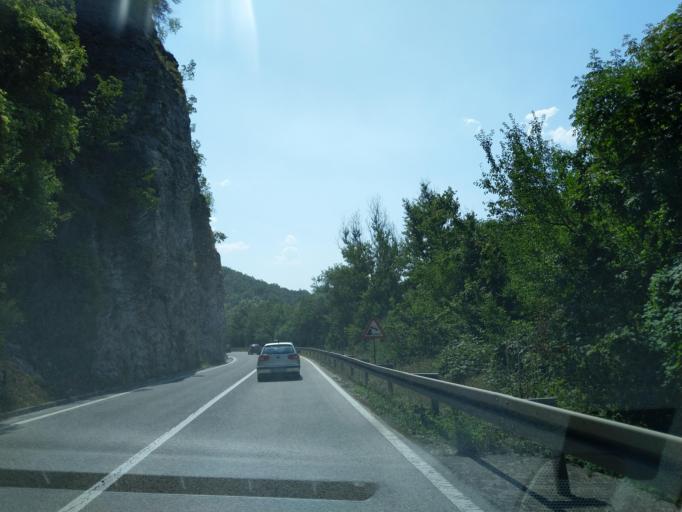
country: RS
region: Central Serbia
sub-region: Zlatiborski Okrug
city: Prijepolje
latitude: 43.4525
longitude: 19.6427
